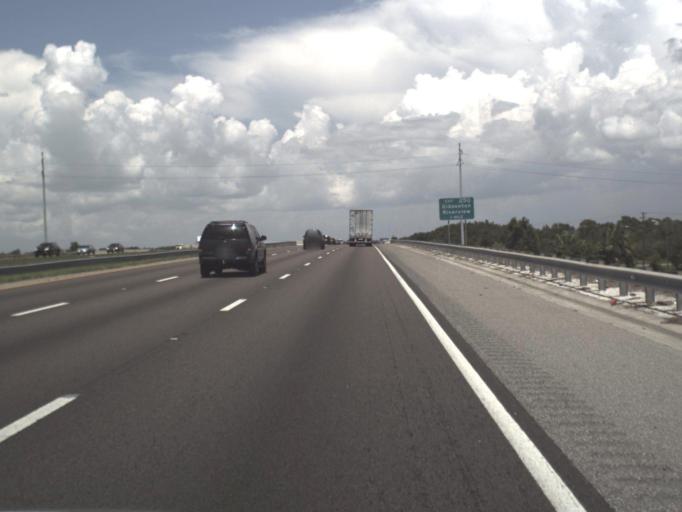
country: US
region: Florida
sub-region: Hillsborough County
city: Gibsonton
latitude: 27.8333
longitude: -82.3497
